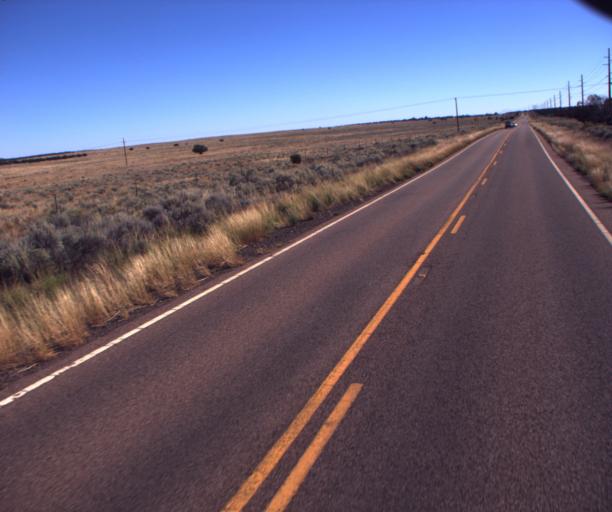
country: US
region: Arizona
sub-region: Navajo County
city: Taylor
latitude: 34.4830
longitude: -110.2834
